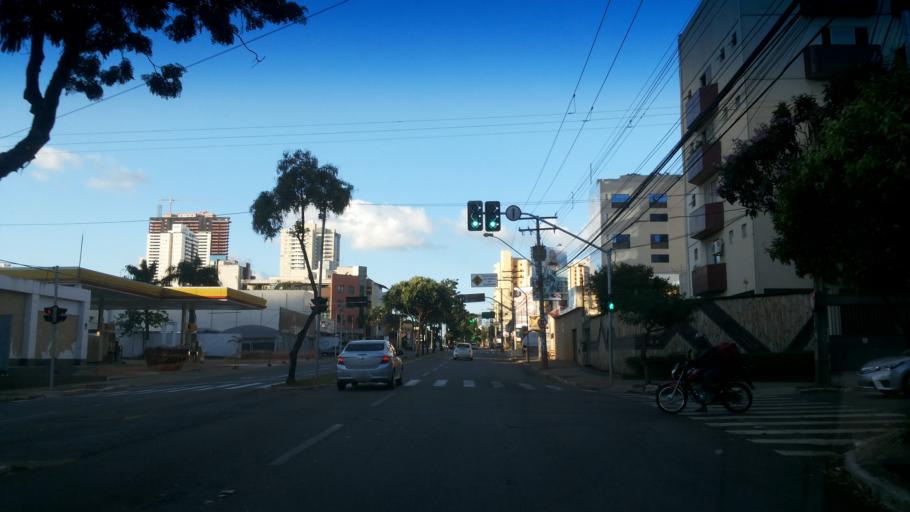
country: BR
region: Goias
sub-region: Goiania
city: Goiania
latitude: -16.7034
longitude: -49.2740
